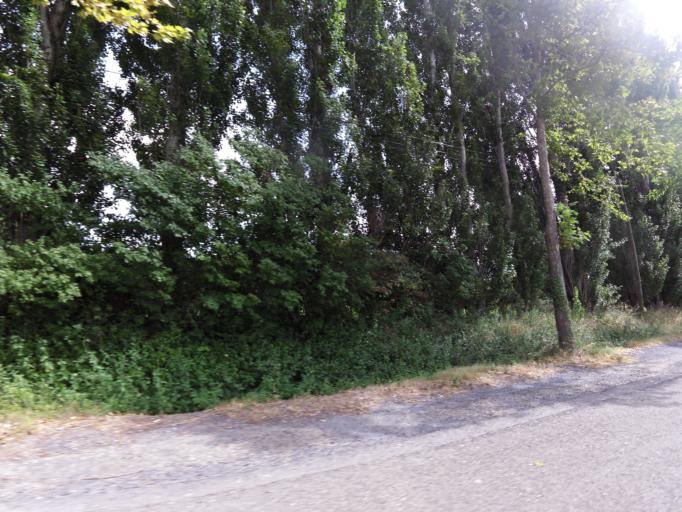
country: FR
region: Languedoc-Roussillon
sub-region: Departement du Gard
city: Saint-Mamert-du-Gard
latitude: 43.8570
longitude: 4.1562
